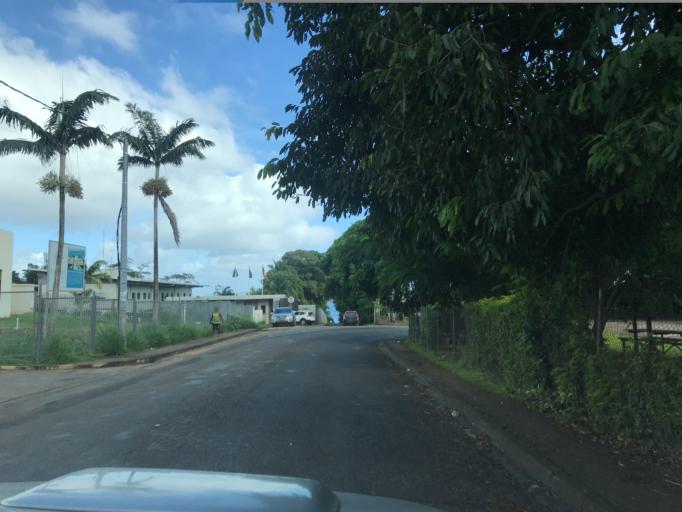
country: VU
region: Shefa
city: Port-Vila
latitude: -17.7426
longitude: 168.3164
